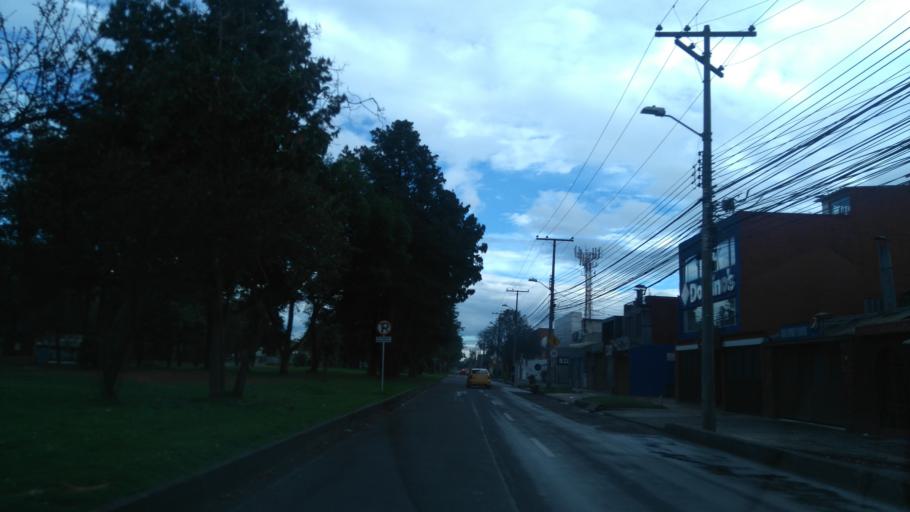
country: CO
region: Bogota D.C.
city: Bogota
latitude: 4.6442
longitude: -74.0915
